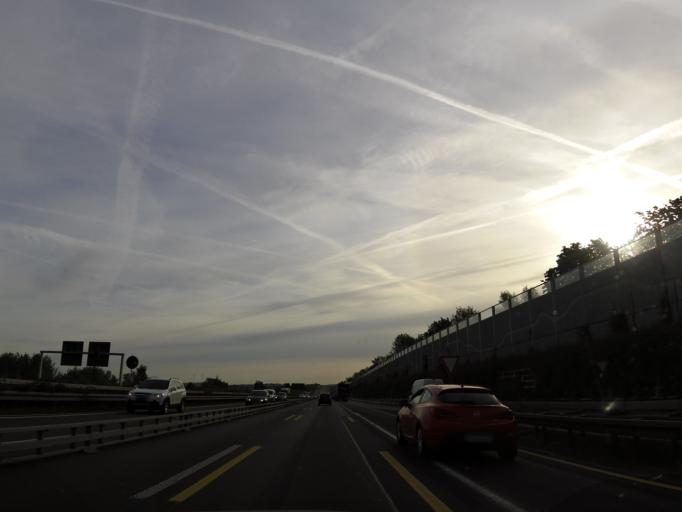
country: DE
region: Hesse
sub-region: Regierungsbezirk Kassel
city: Lohfelden
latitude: 51.2776
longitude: 9.5323
